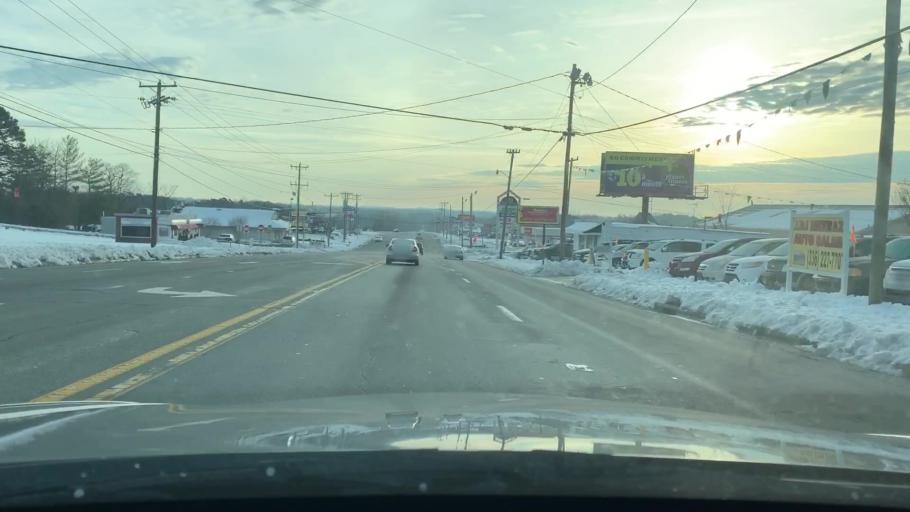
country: US
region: North Carolina
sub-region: Alamance County
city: Haw River
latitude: 36.0908
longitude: -79.3854
